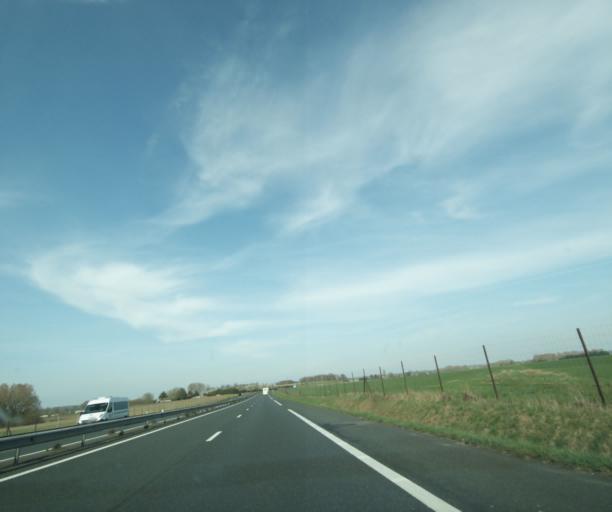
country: FR
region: Centre
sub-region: Departement de l'Indre
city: Vatan
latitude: 47.0754
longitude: 1.8244
